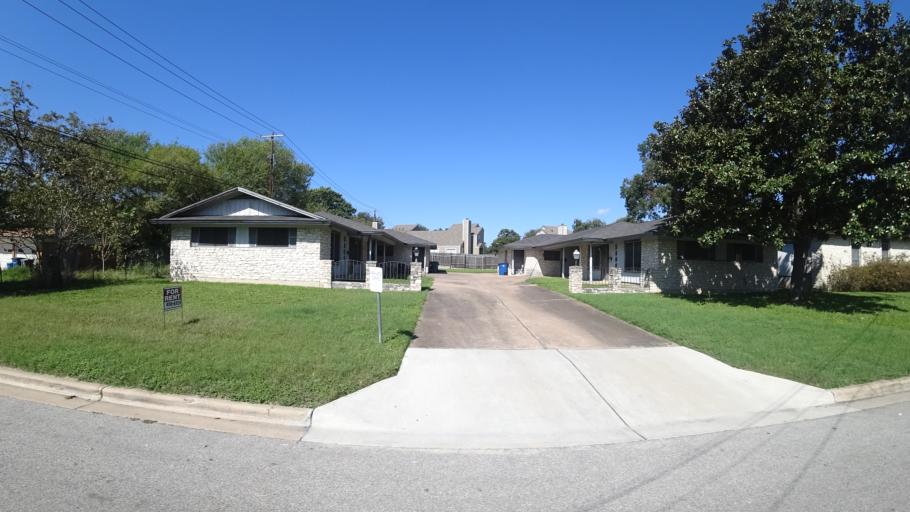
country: US
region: Texas
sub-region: Travis County
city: Austin
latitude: 30.3152
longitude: -97.6989
